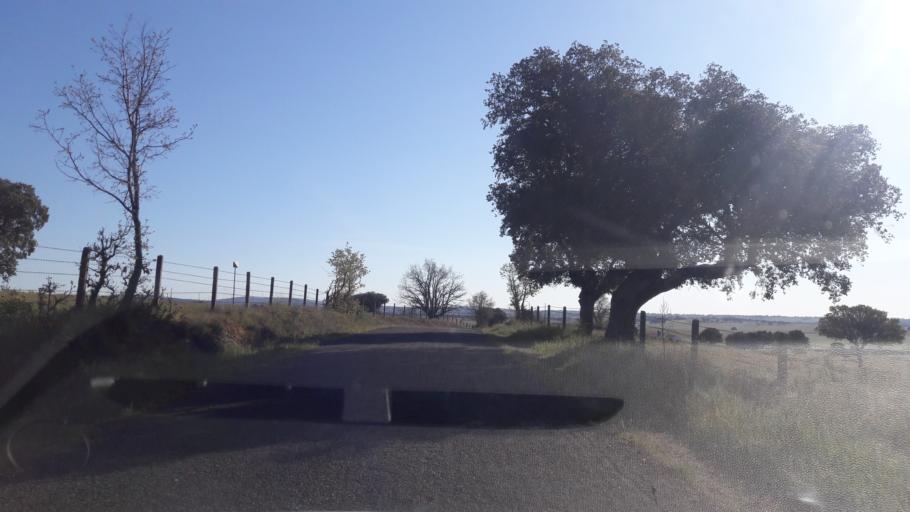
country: ES
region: Castille and Leon
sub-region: Provincia de Salamanca
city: Monleon
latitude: 40.6092
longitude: -5.8291
